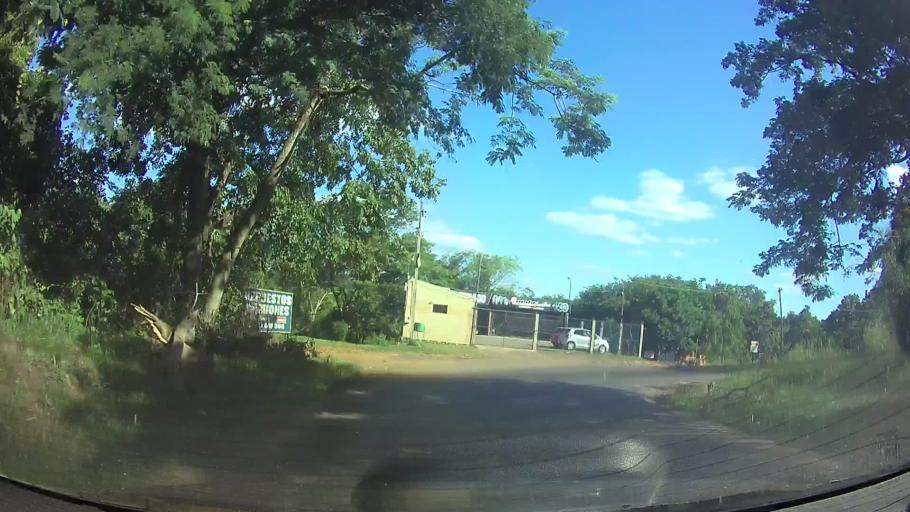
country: PY
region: Cordillera
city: Caacupe
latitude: -25.3786
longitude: -57.1362
